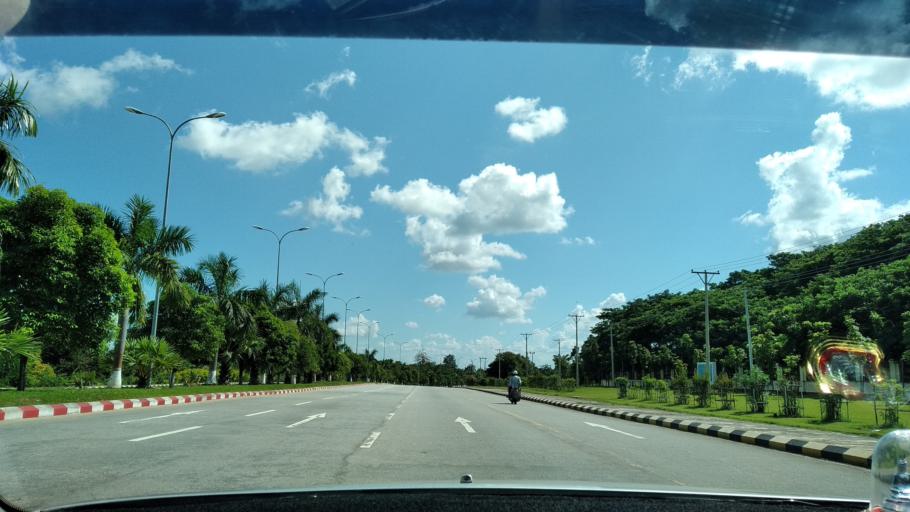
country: MM
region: Mandalay
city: Nay Pyi Taw
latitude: 19.7842
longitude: 96.1444
